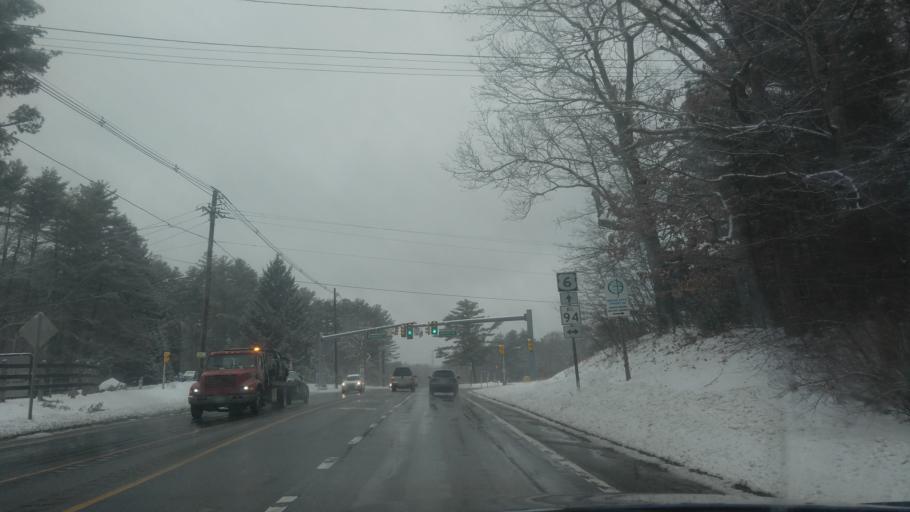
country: US
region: Rhode Island
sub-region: Providence County
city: Foster
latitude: 41.8151
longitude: -71.7331
